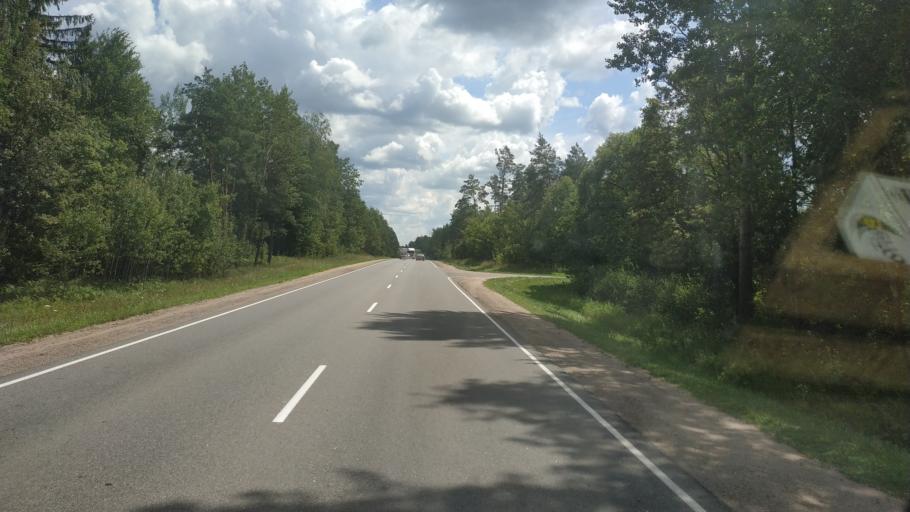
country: BY
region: Mogilev
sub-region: Mahilyowski Rayon
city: Veyno
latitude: 53.8246
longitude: 30.4239
